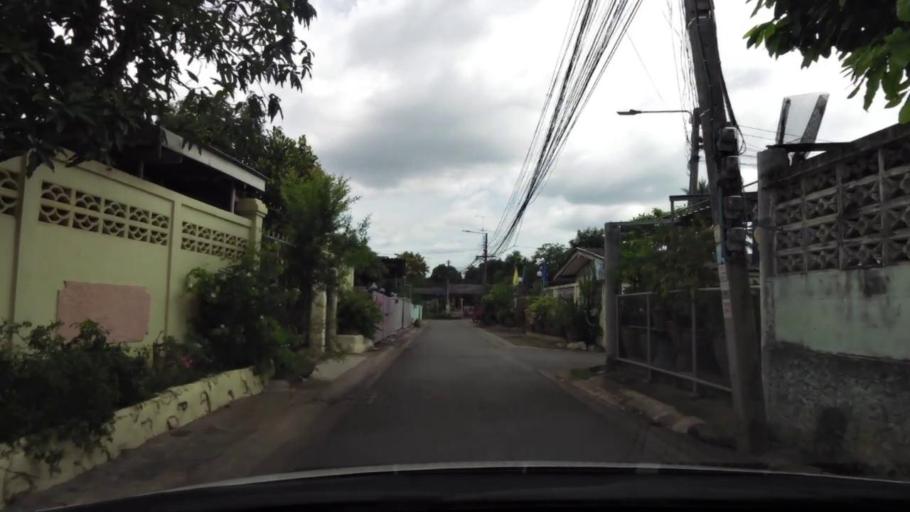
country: TH
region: Ratchaburi
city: Ratchaburi
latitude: 13.5321
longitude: 99.8313
